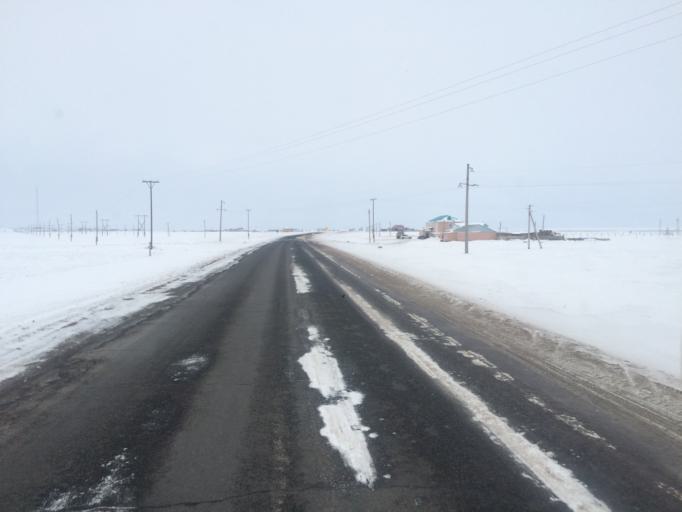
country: RU
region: Orenburg
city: Dombarovskiy
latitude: 49.9582
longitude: 60.0822
